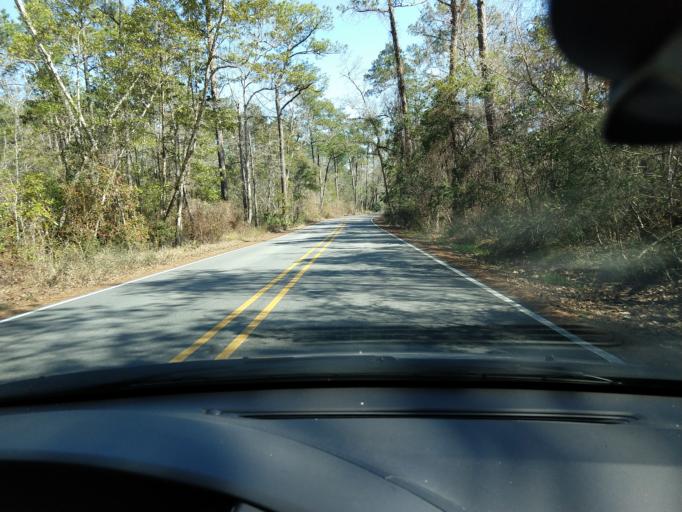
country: US
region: Mississippi
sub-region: Jackson County
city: Gulf Park Estates
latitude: 30.3961
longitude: -88.7861
